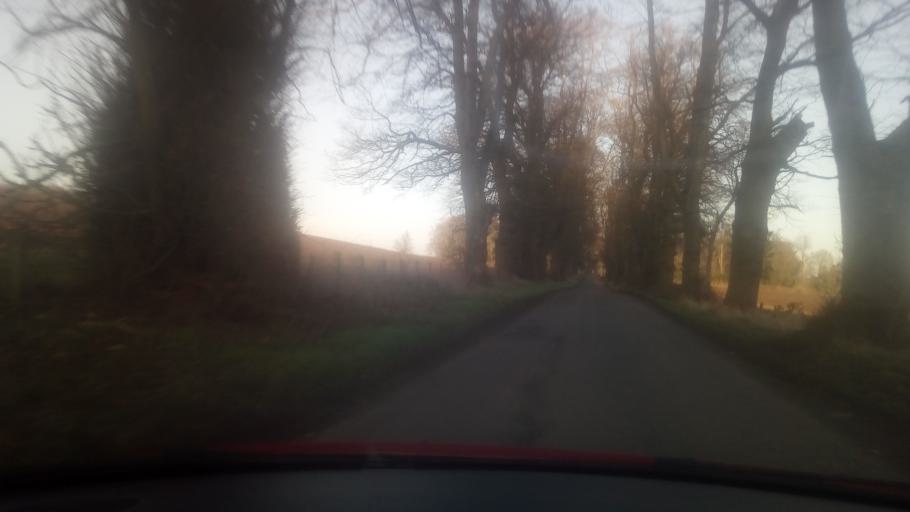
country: GB
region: Scotland
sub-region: The Scottish Borders
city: Jedburgh
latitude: 55.5231
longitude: -2.5257
